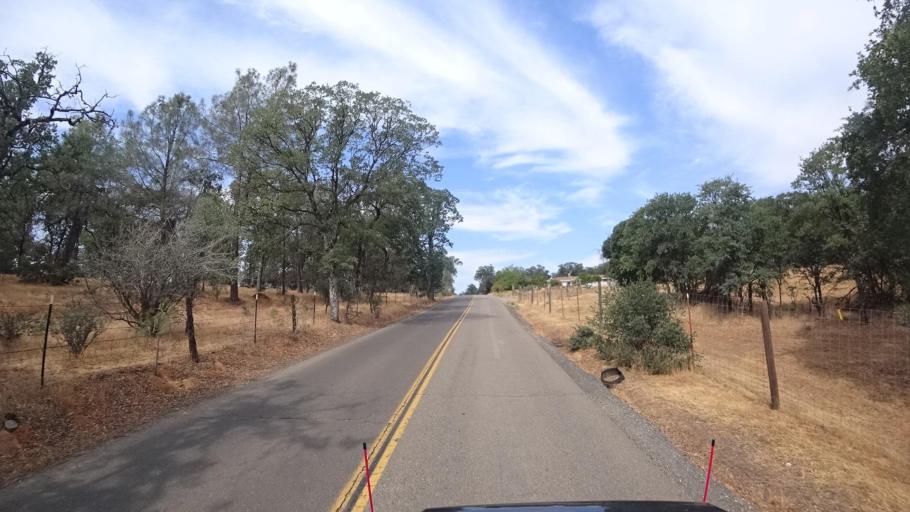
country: US
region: California
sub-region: Mariposa County
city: Midpines
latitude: 37.5341
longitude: -119.9625
